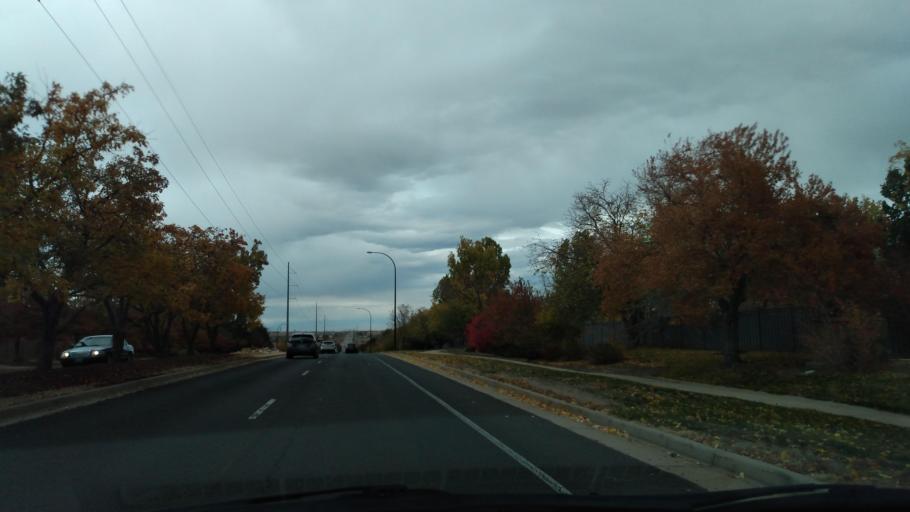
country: US
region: Colorado
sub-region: Adams County
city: Northglenn
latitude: 39.9345
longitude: -104.9780
